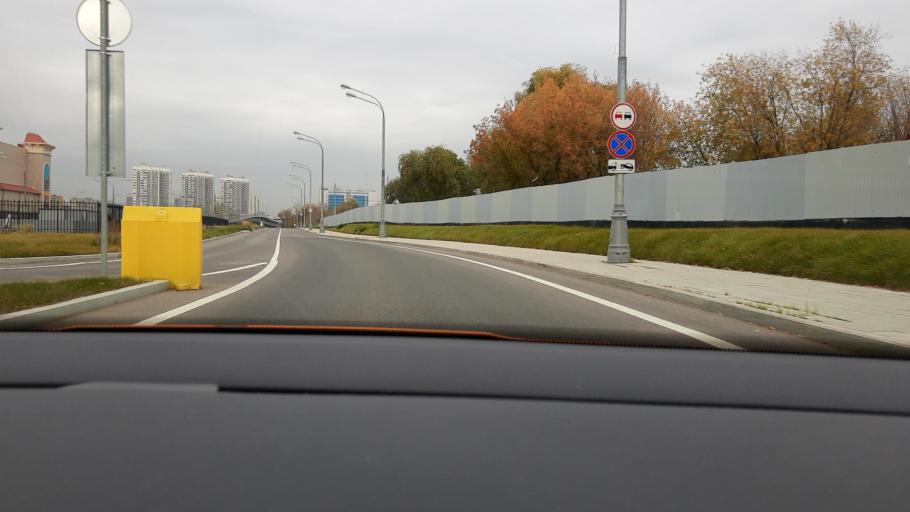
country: RU
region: Moskovskaya
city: Kozhukhovo
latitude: 55.6921
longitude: 37.6805
